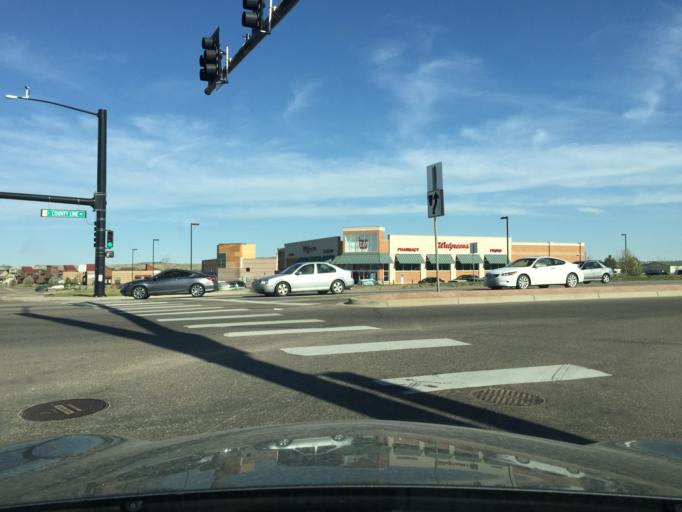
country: US
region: Colorado
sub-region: Boulder County
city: Erie
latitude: 40.0364
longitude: -105.0558
